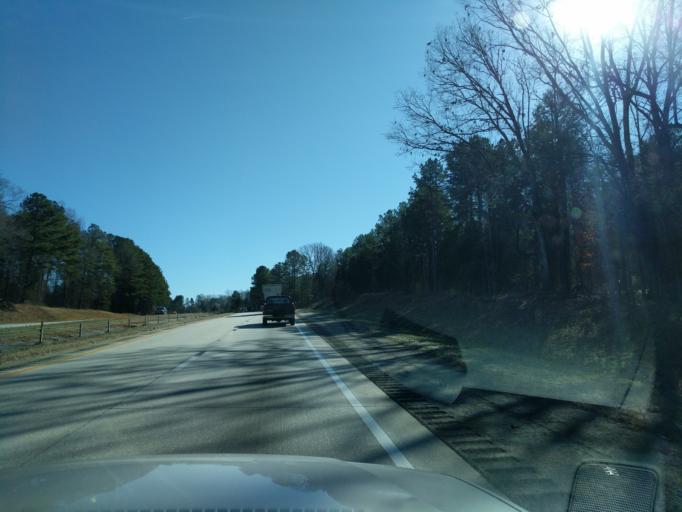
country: US
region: South Carolina
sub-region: Laurens County
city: Clinton
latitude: 34.5196
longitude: -81.9084
